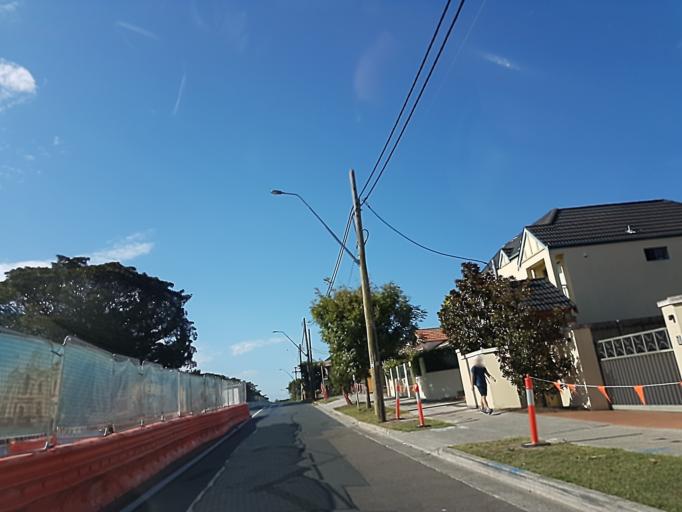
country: AU
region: New South Wales
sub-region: Randwick
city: Kingsford
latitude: -33.9157
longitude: 151.2349
